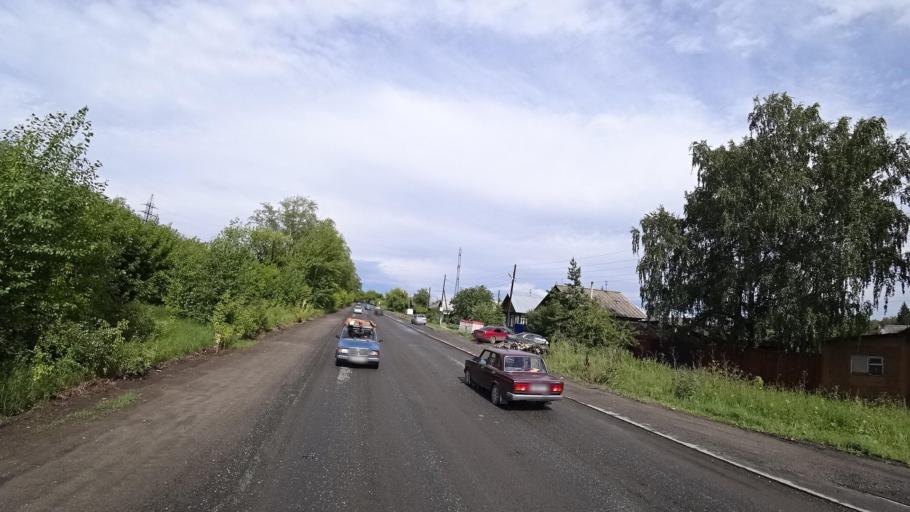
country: RU
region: Sverdlovsk
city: Kamyshlov
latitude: 56.8452
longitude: 62.7504
